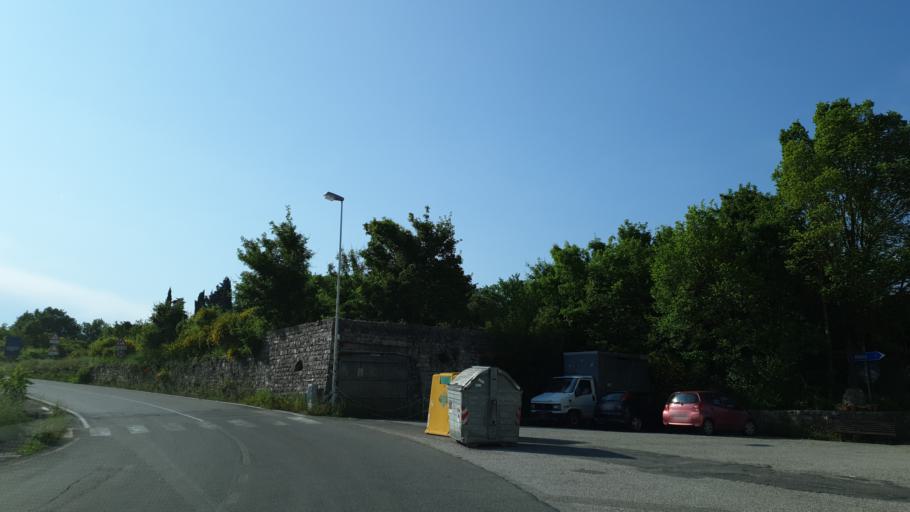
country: IT
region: Tuscany
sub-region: Province of Arezzo
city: Strada
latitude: 43.7523
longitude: 11.7228
